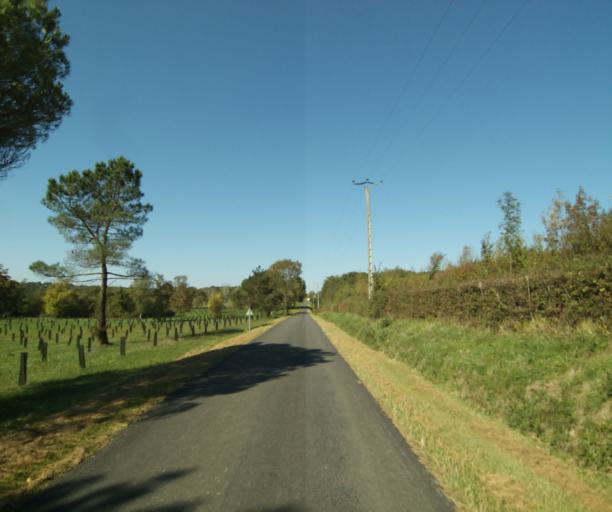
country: FR
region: Midi-Pyrenees
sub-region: Departement du Gers
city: Cazaubon
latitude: 43.9330
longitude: -0.0231
